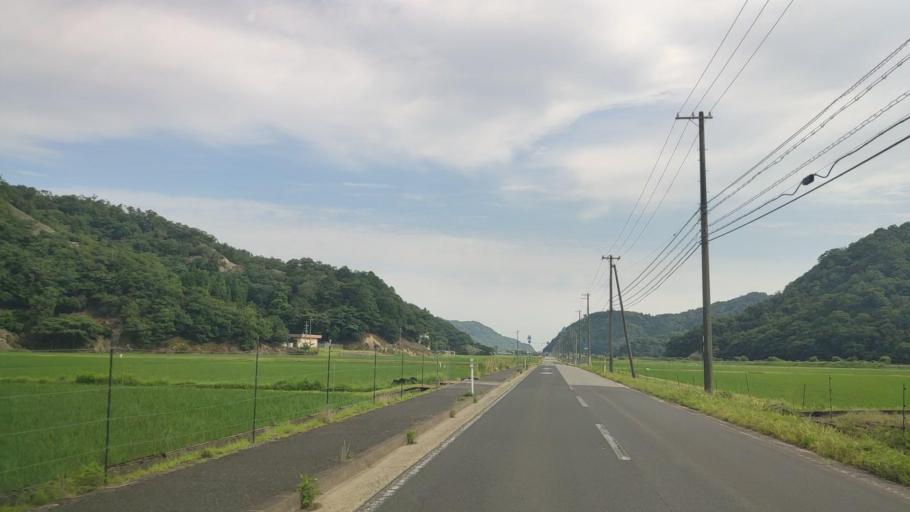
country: JP
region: Hyogo
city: Toyooka
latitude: 35.6223
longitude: 134.8413
